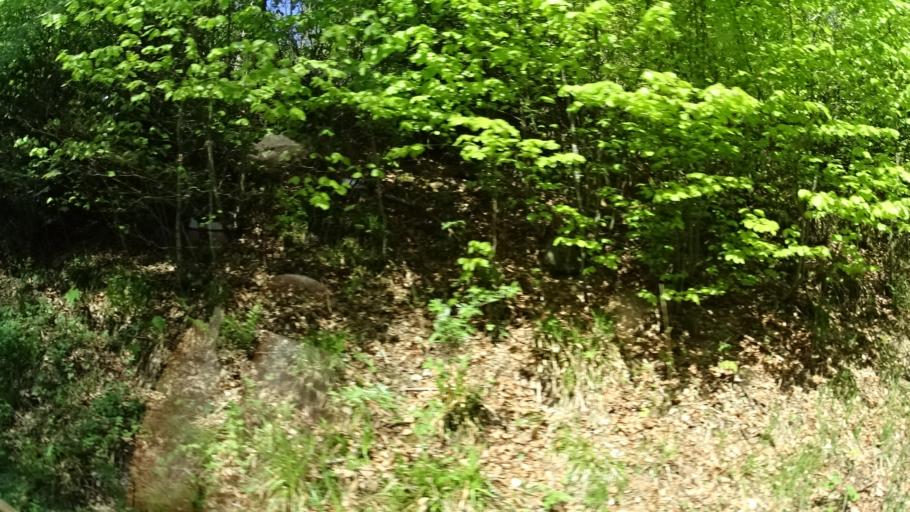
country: DE
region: Baden-Wuerttemberg
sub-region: Karlsruhe Region
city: Hofen an der Enz
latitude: 48.7886
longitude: 8.5476
